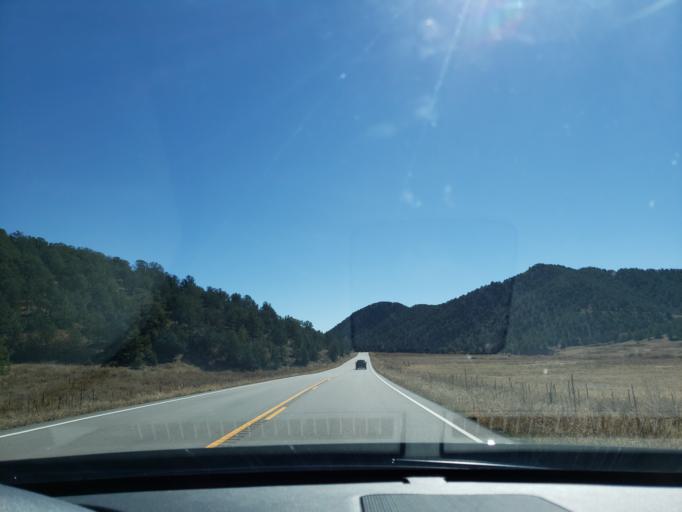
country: US
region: Colorado
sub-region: Fremont County
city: Canon City
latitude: 38.6277
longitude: -105.4588
